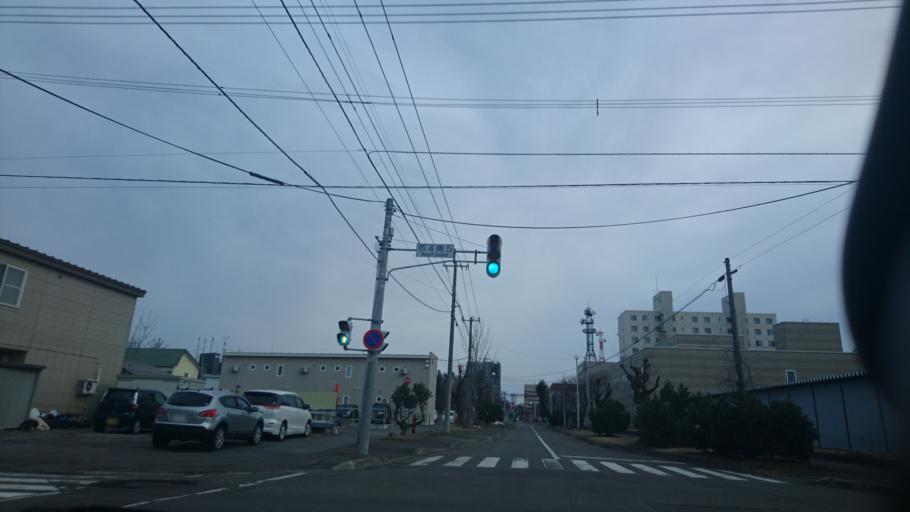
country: JP
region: Hokkaido
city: Obihiro
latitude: 42.9270
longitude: 143.1983
